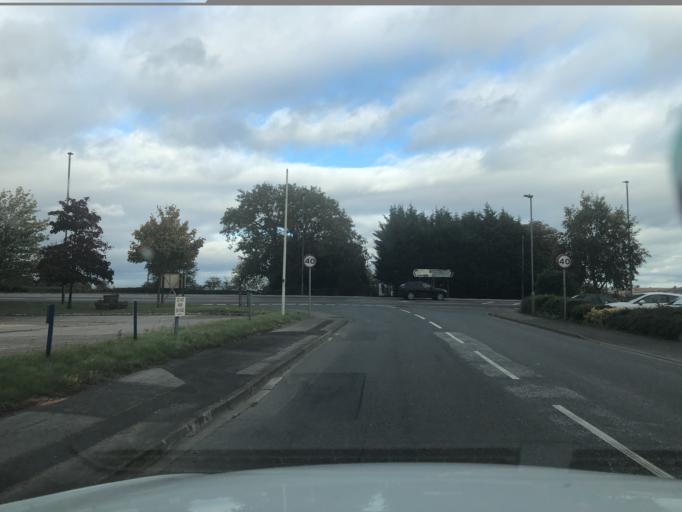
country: GB
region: England
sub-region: North Yorkshire
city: Northallerton
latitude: 54.3509
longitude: -1.4467
